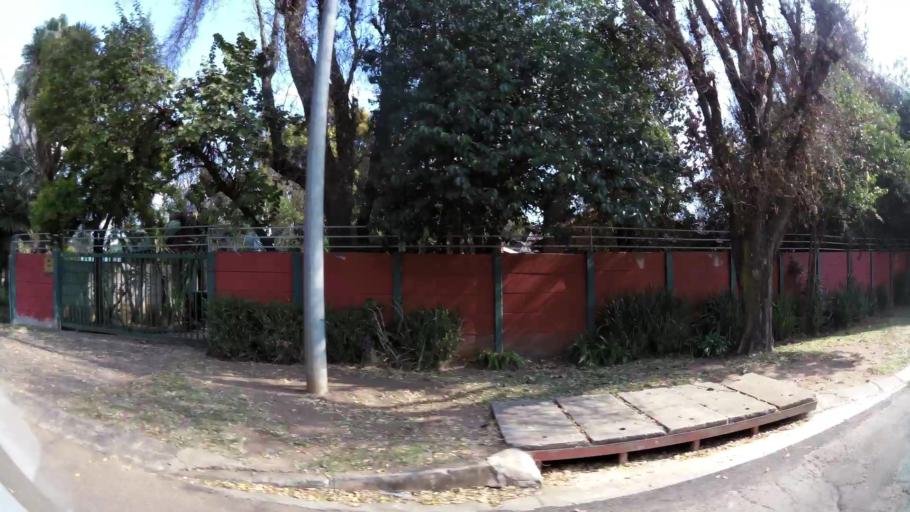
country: ZA
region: Gauteng
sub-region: Ekurhuleni Metropolitan Municipality
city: Tembisa
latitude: -26.0847
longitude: 28.2691
